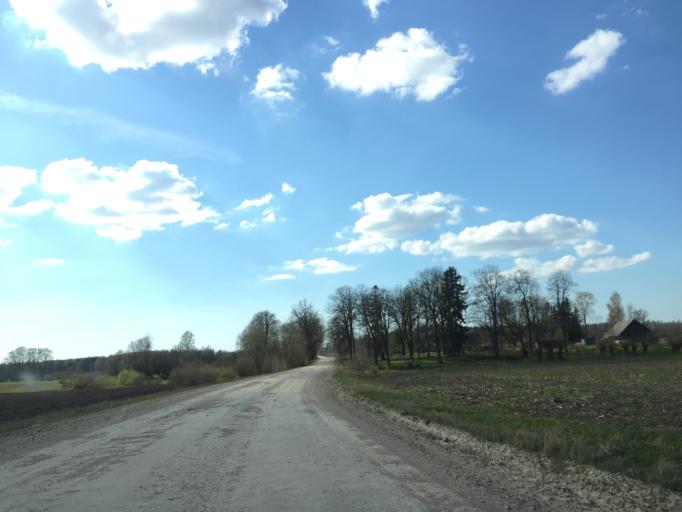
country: LV
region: Krimulda
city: Ragana
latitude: 57.3401
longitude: 24.6204
